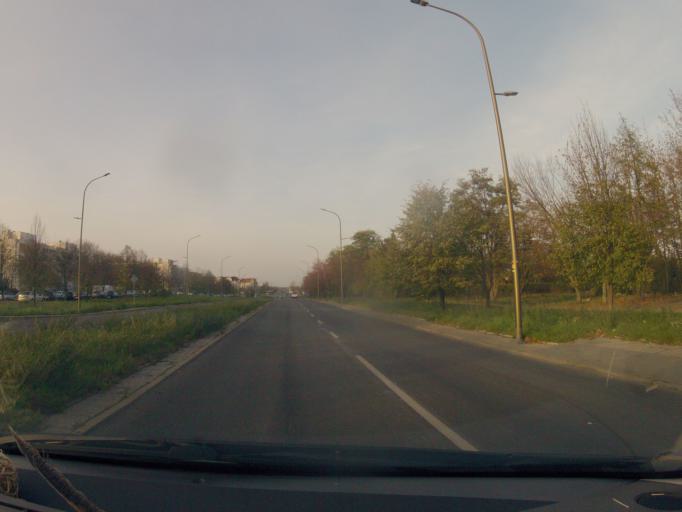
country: PL
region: Opole Voivodeship
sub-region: Powiat opolski
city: Opole
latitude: 50.6724
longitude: 17.9754
